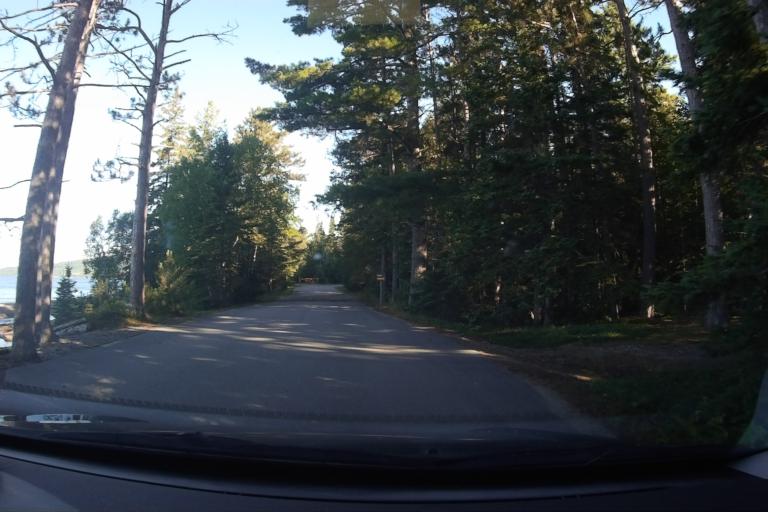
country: CA
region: Ontario
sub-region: Algoma
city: Sault Ste. Marie
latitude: 47.3329
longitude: -84.6157
